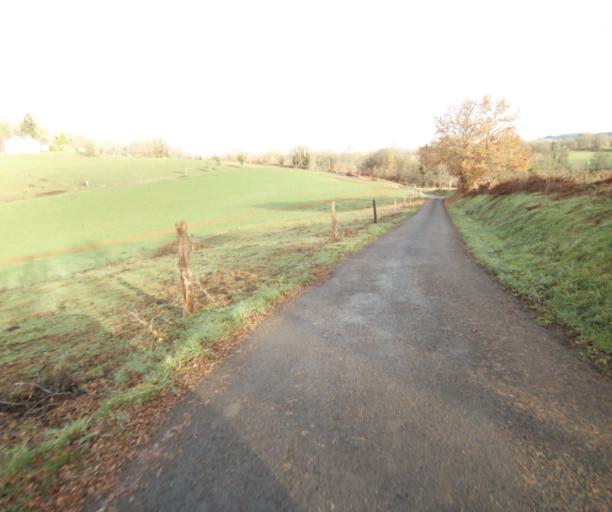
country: FR
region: Limousin
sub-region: Departement de la Correze
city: Sainte-Fereole
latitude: 45.2504
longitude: 1.6050
